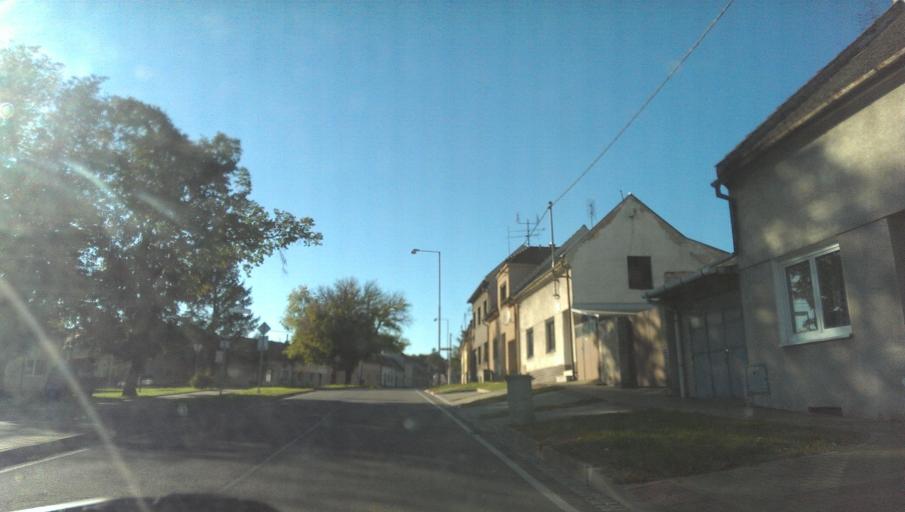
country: CZ
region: Zlin
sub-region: Okres Uherske Hradiste
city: Stare Mesto
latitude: 49.0801
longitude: 17.4441
